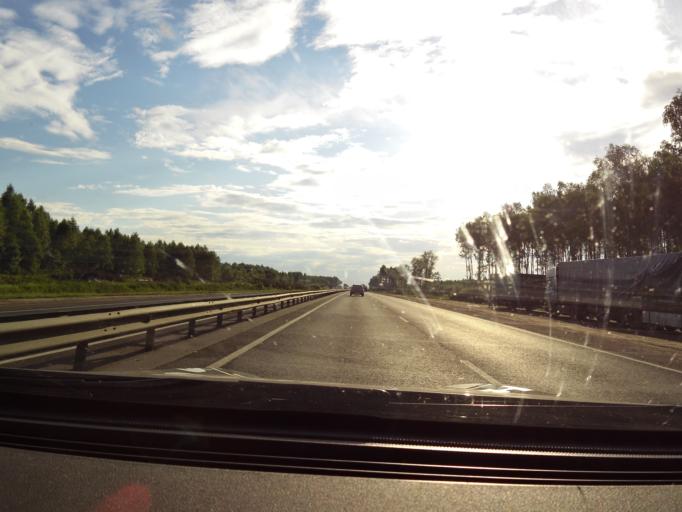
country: RU
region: Vladimir
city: Melekhovo
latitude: 56.2047
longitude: 41.1649
